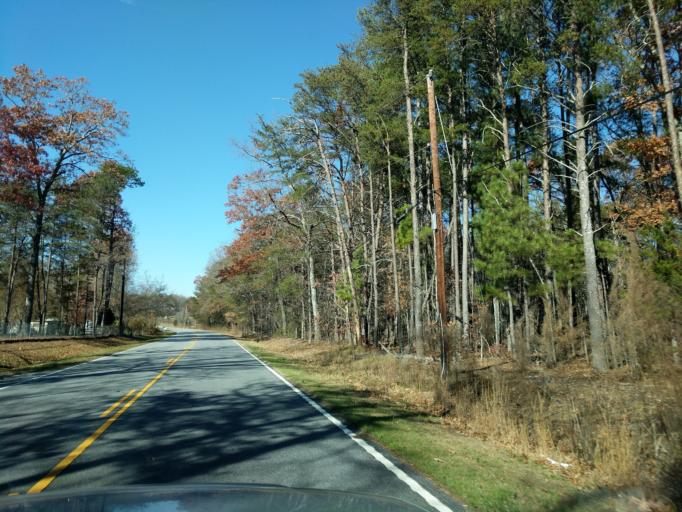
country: US
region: South Carolina
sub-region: Spartanburg County
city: Inman Mills
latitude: 35.0732
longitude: -82.1957
